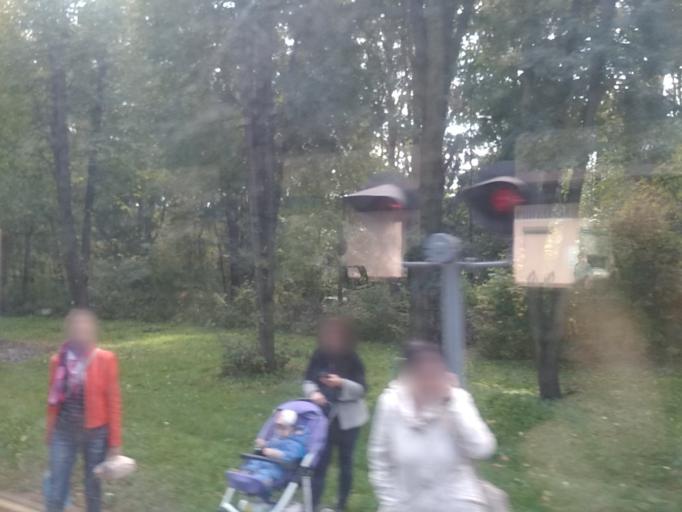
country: BY
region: Minsk
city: Machulishchy
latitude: 53.7847
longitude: 27.6048
